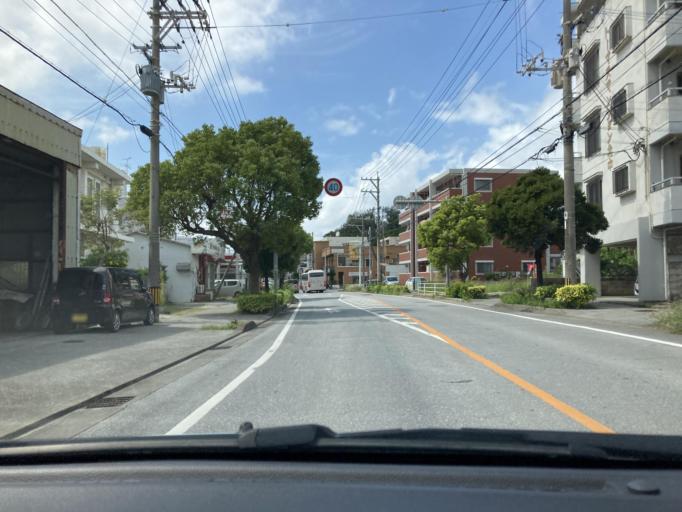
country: JP
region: Okinawa
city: Chatan
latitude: 26.3013
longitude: 127.7984
